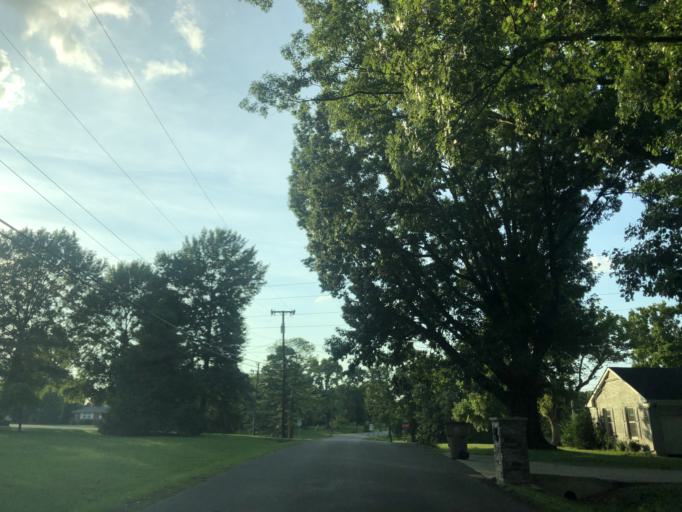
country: US
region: Tennessee
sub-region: Davidson County
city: Nashville
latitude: 36.1586
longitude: -86.7036
